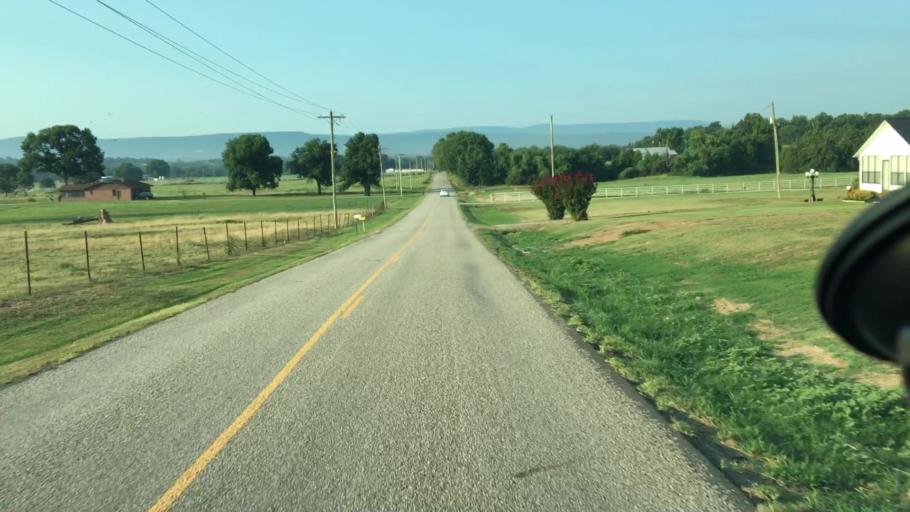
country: US
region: Arkansas
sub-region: Johnson County
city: Coal Hill
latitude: 35.3456
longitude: -93.6135
